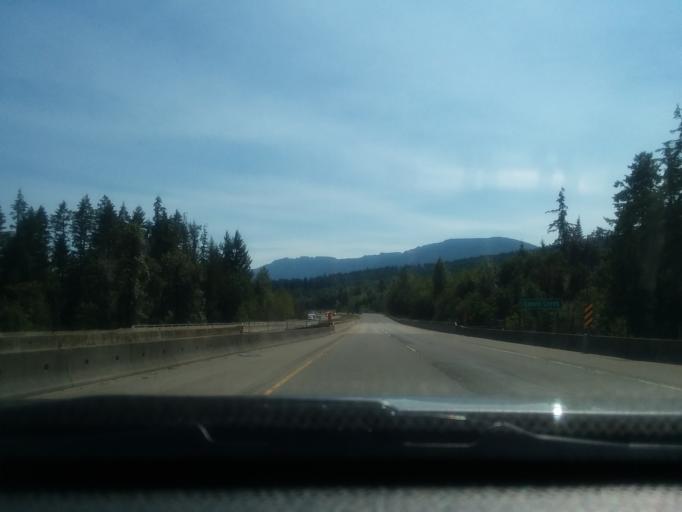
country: CA
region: British Columbia
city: Cumberland
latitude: 49.4975
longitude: -124.8394
